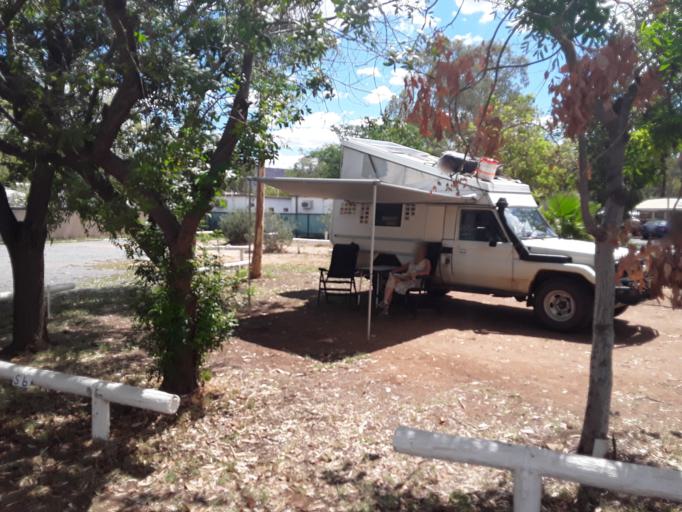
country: AU
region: Northern Territory
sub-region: Alice Springs
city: Alice Springs
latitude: -23.6994
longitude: 133.8619
